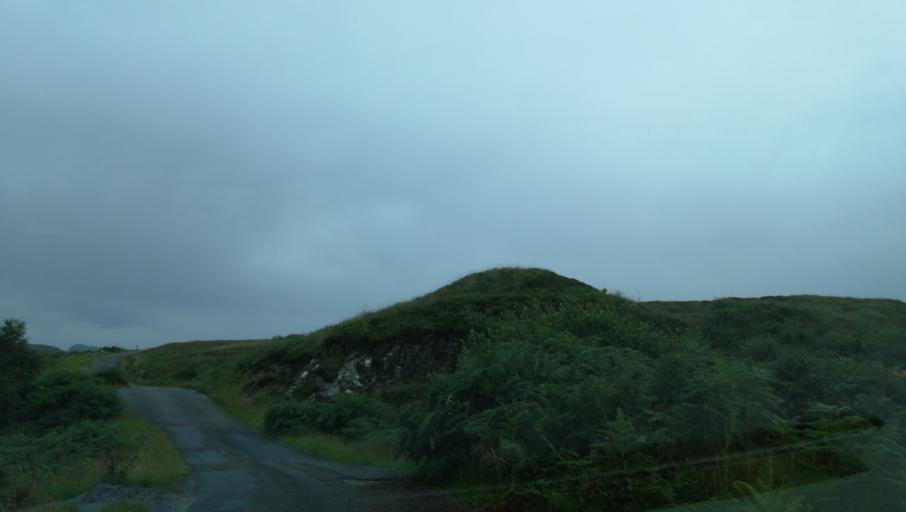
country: GB
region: Scotland
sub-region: Argyll and Bute
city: Isle Of Mull
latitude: 56.7125
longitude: -6.1448
